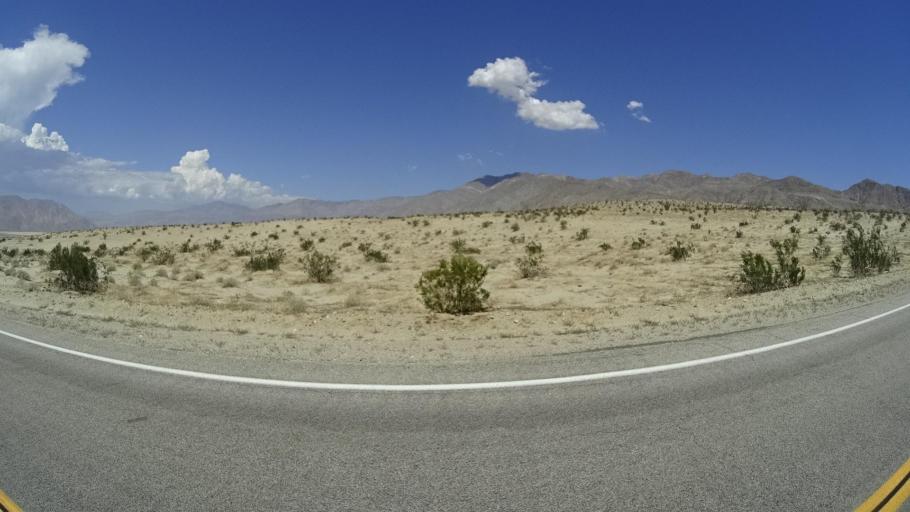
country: US
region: California
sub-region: San Diego County
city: Borrego Springs
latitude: 33.3054
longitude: -116.2117
